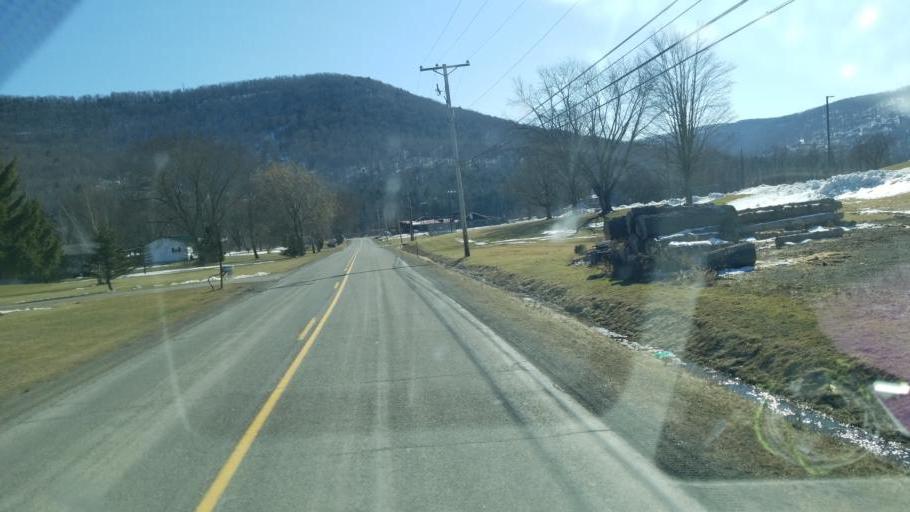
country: US
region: Pennsylvania
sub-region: Tioga County
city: Westfield
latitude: 41.9204
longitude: -77.5649
